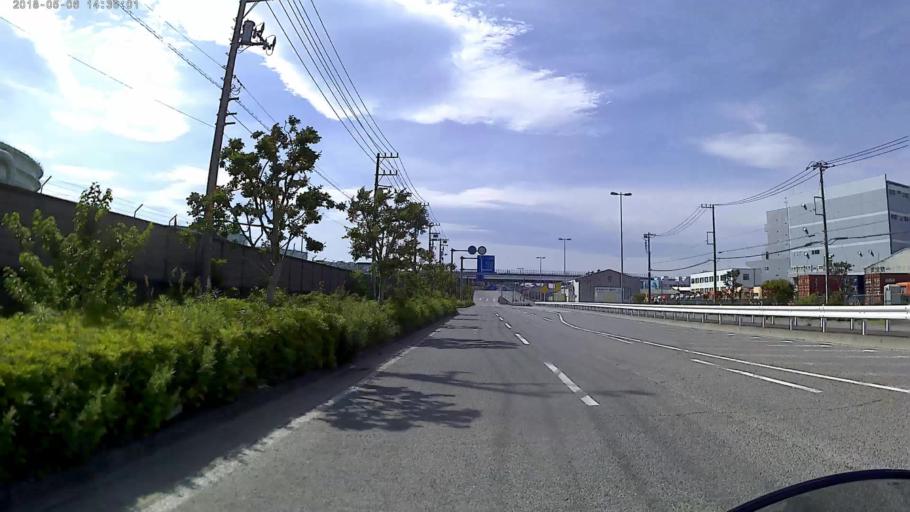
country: JP
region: Kanagawa
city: Yokohama
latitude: 35.4133
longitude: 139.6718
